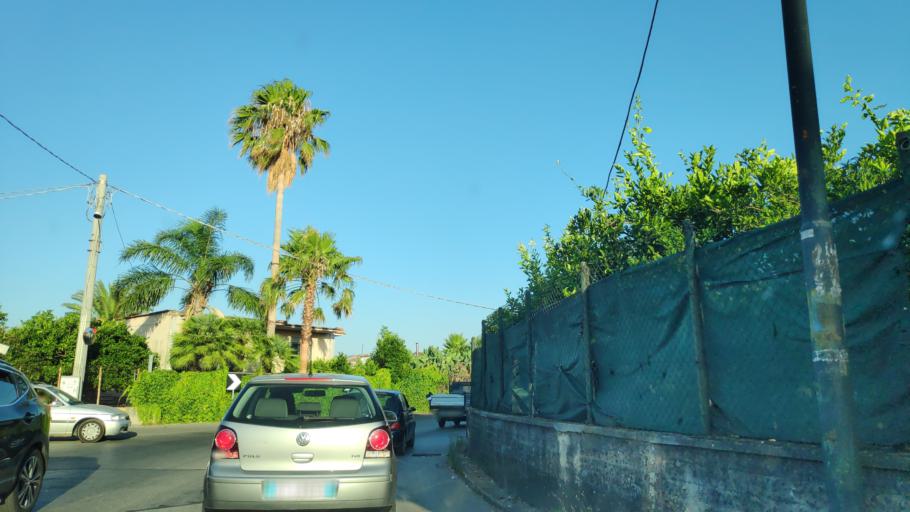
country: IT
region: Campania
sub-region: Provincia di Salerno
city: Pagani
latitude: 40.7628
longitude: 14.6151
